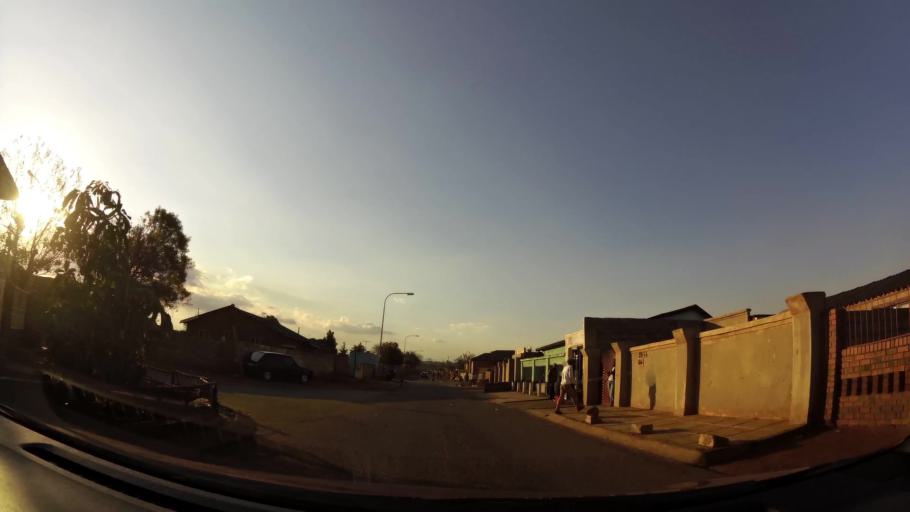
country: ZA
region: Gauteng
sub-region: City of Johannesburg Metropolitan Municipality
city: Soweto
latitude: -26.2236
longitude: 27.8569
